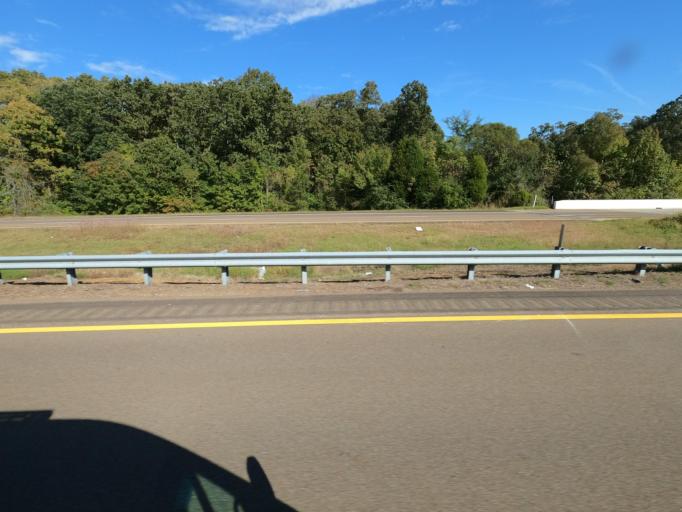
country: US
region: Tennessee
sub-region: Shelby County
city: Arlington
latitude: 35.3115
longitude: -89.7210
